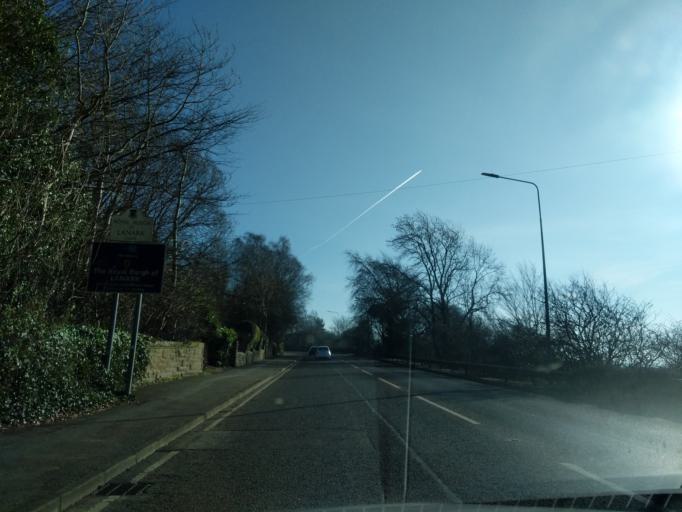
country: GB
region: Scotland
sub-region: South Lanarkshire
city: Lanark
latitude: 55.6766
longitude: -3.7951
